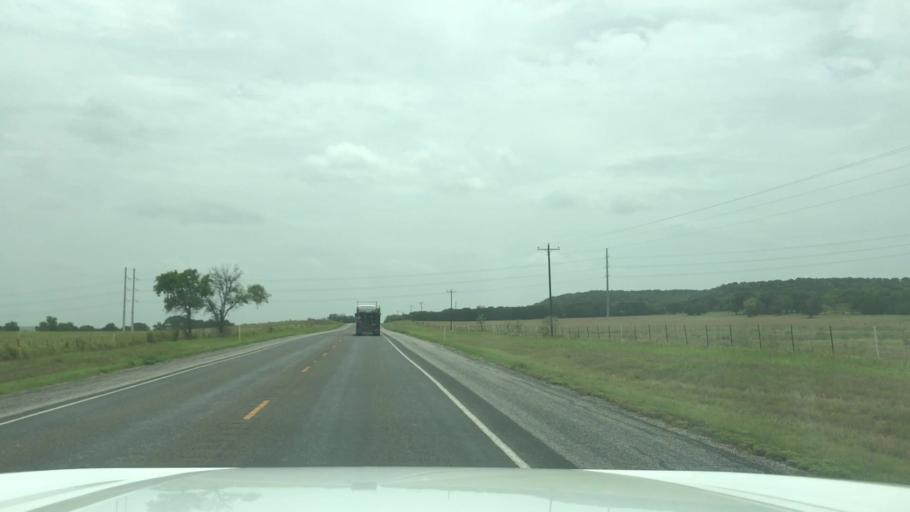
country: US
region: Texas
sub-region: Bosque County
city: Meridian
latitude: 31.8761
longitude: -97.6406
